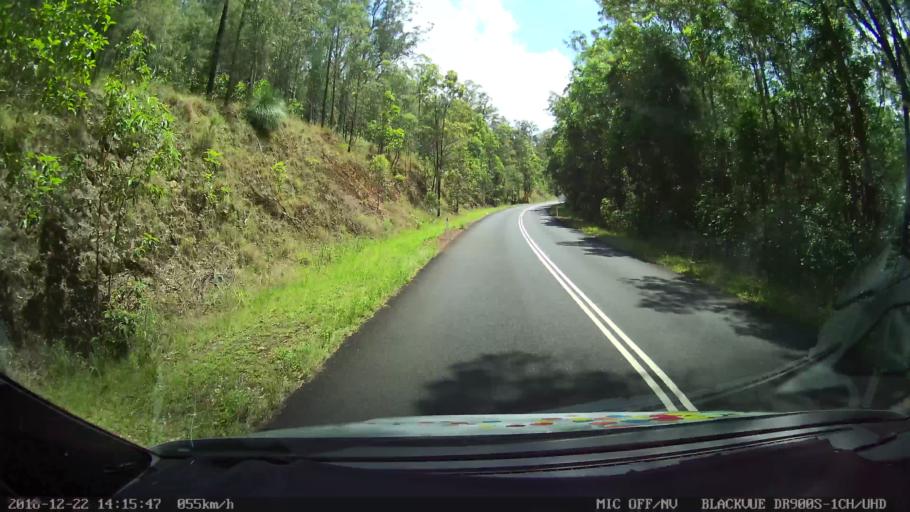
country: AU
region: New South Wales
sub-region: Clarence Valley
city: Coutts Crossing
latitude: -30.0029
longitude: 152.6753
